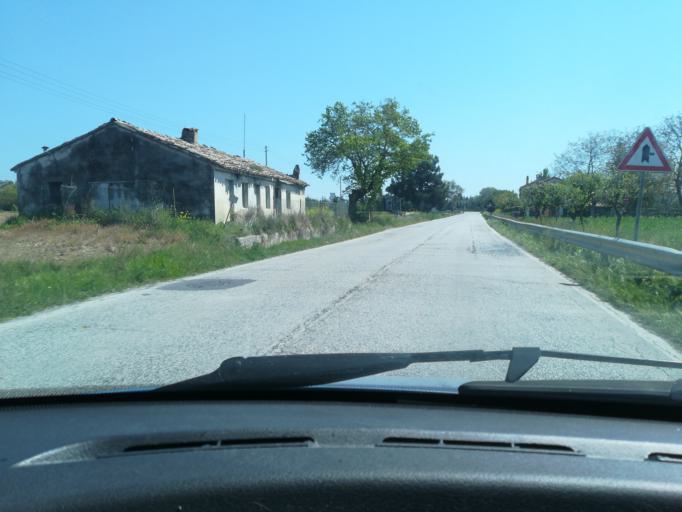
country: IT
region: The Marches
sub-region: Provincia di Ancona
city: Castelfidardo
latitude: 43.4534
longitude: 13.5271
